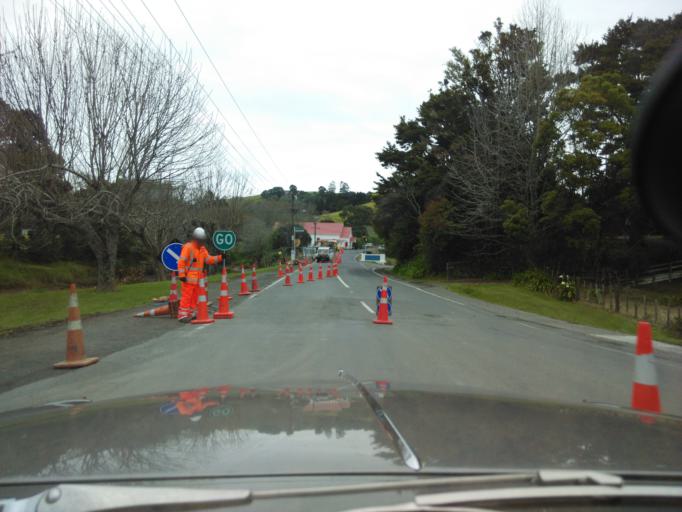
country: NZ
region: Auckland
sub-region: Auckland
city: Warkworth
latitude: -36.5124
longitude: 174.6615
